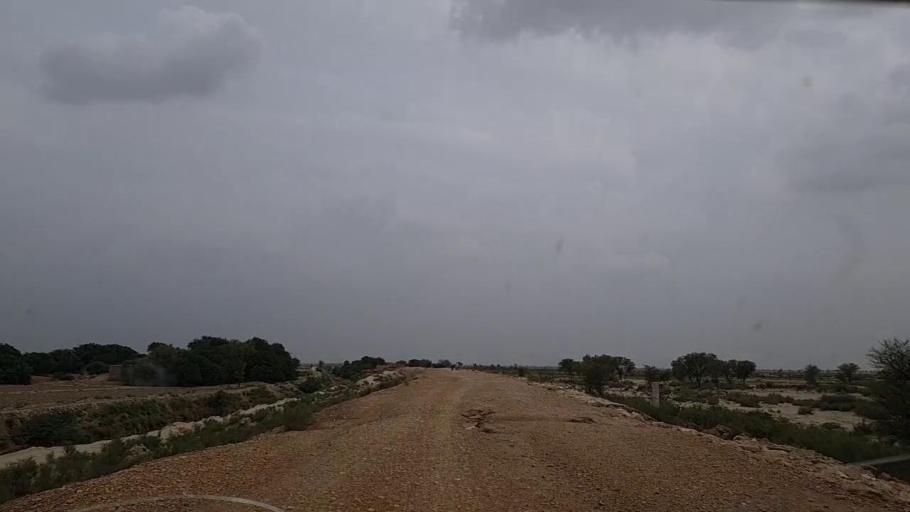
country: PK
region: Sindh
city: Johi
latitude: 26.7224
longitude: 67.5786
